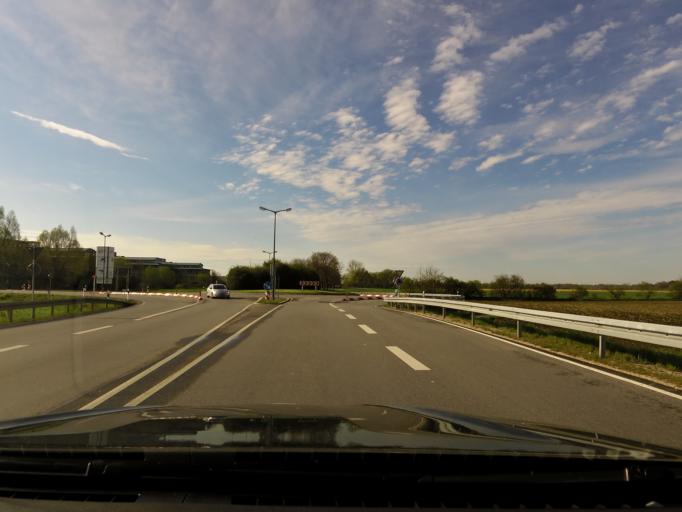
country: DE
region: Bavaria
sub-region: Upper Bavaria
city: Hallbergmoos
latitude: 48.3344
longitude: 11.7297
